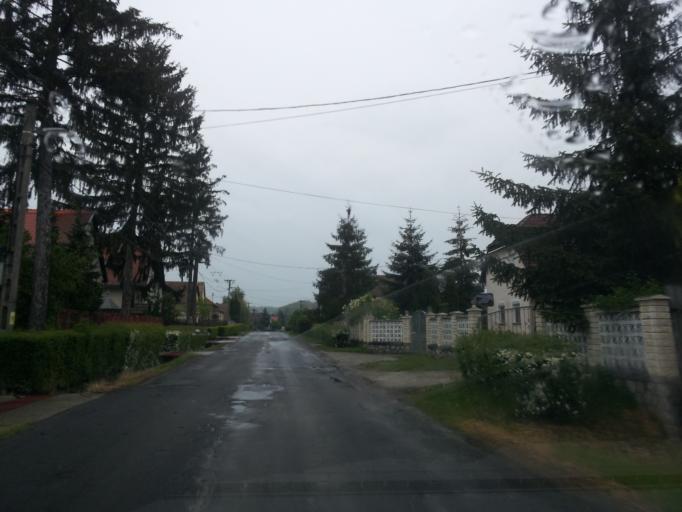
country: HU
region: Tolna
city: Szentgalpuszta
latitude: 46.2789
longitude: 18.6419
